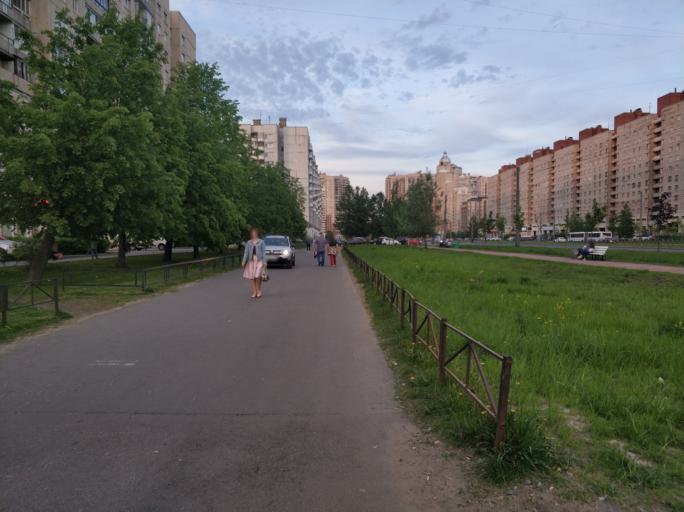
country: RU
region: St.-Petersburg
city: Novaya Derevnya
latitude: 60.0000
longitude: 30.2874
